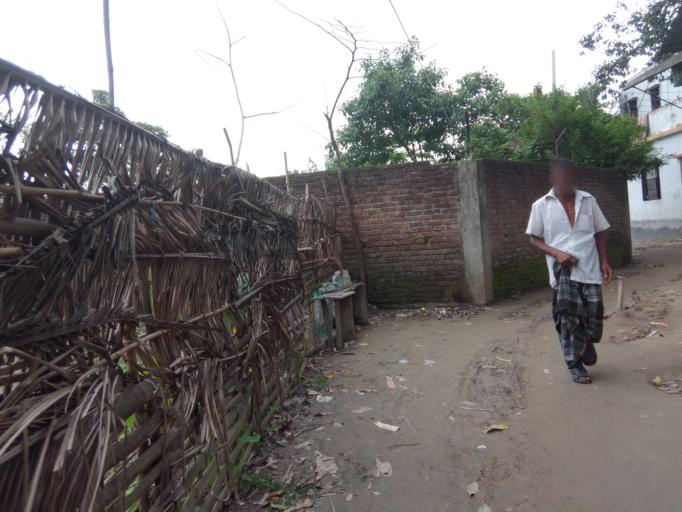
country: BD
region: Dhaka
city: Paltan
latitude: 23.7514
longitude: 90.4481
